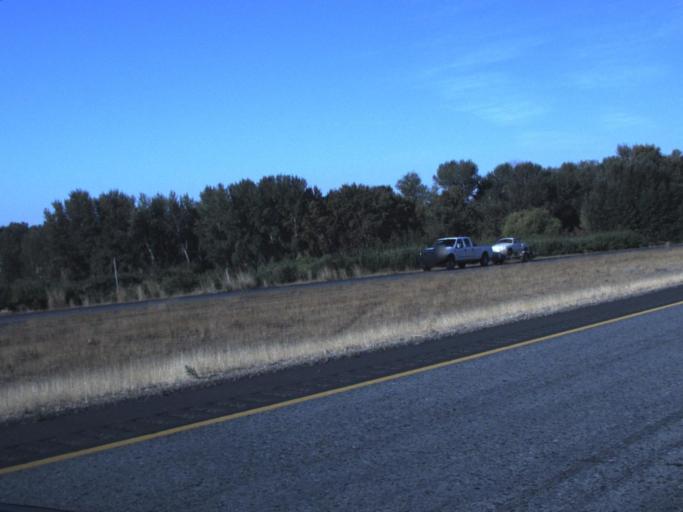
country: US
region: Washington
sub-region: Yakima County
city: Wapato
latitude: 46.4907
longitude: -120.4256
